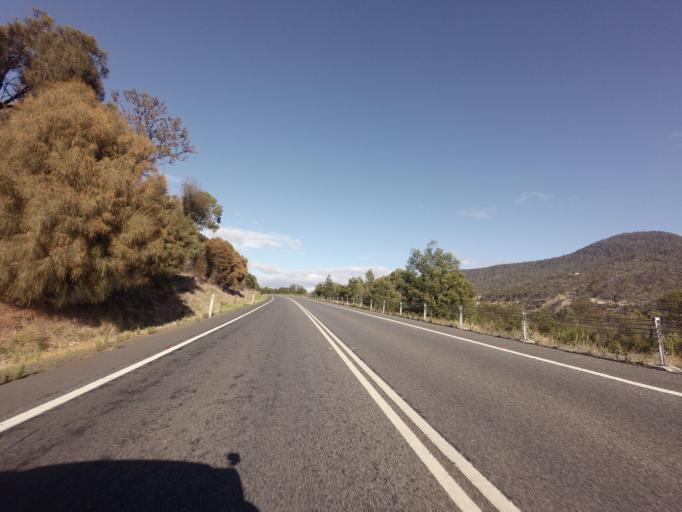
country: AU
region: Tasmania
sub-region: Glenorchy
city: Granton
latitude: -42.7578
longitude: 147.1513
